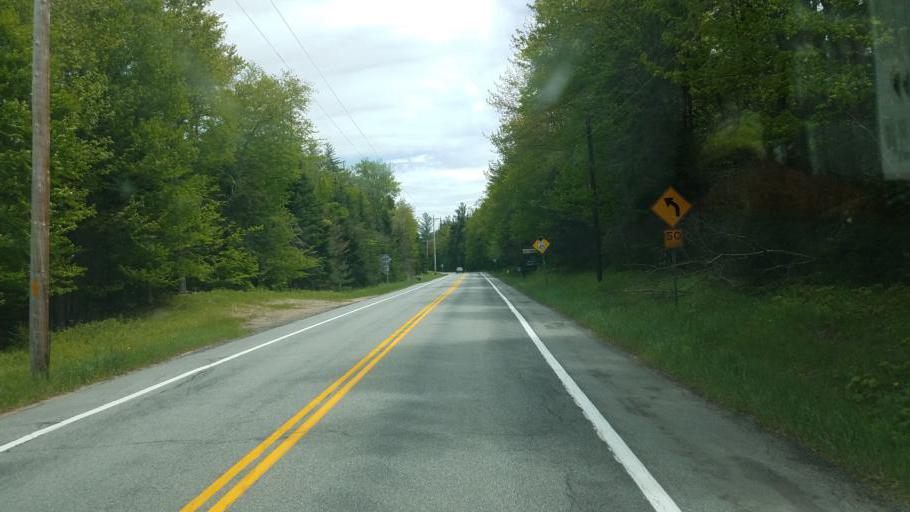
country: US
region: New York
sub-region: Hamilton County
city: Lake Pleasant
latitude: 43.8062
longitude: -74.6614
